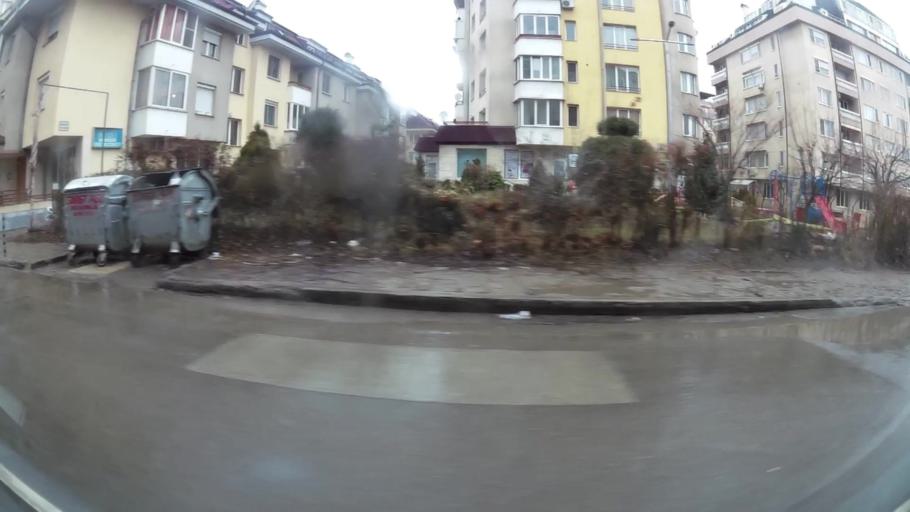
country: BG
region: Sofia-Capital
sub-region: Stolichna Obshtina
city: Sofia
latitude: 42.6478
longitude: 23.3700
